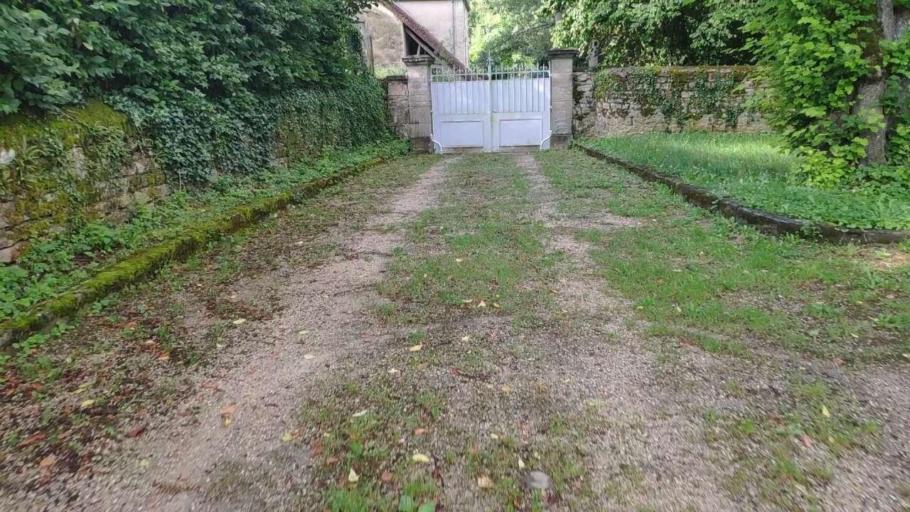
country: FR
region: Franche-Comte
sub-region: Departement du Jura
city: Poligny
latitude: 46.7977
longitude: 5.6176
